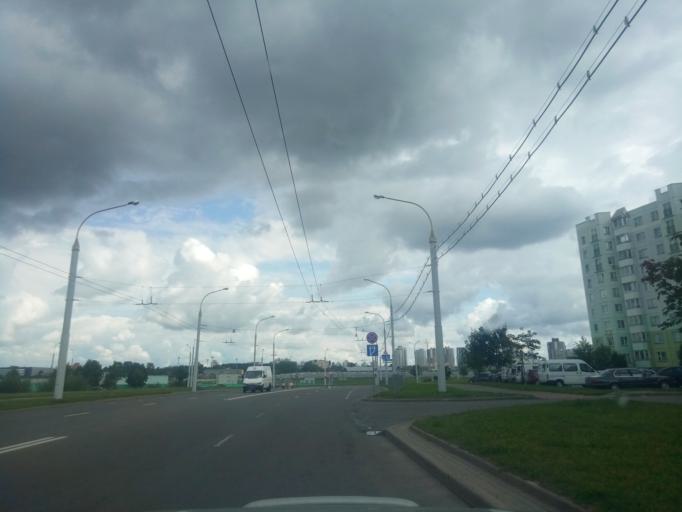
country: BY
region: Minsk
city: Novoye Medvezhino
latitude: 53.8940
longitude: 27.4153
